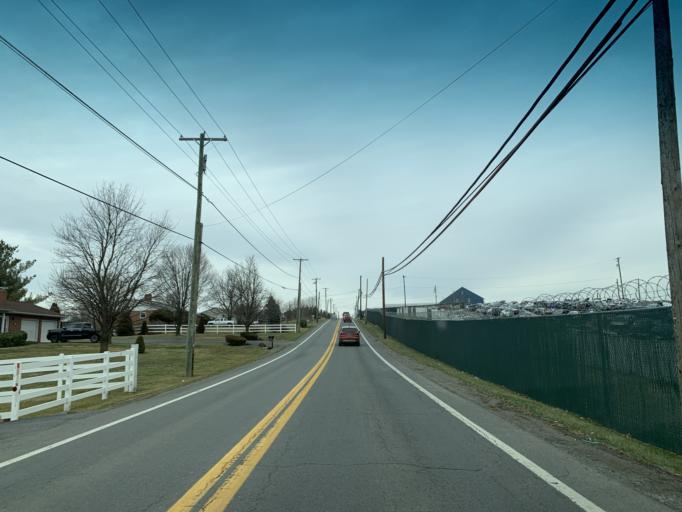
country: US
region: West Virginia
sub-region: Berkeley County
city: Martinsburg
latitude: 39.5303
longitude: -77.9160
